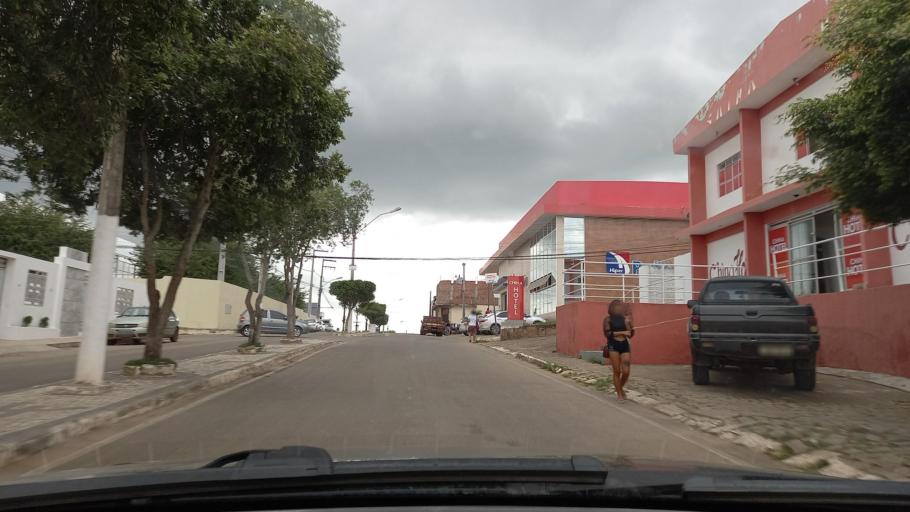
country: BR
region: Sergipe
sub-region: Caninde De Sao Francisco
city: Caninde de Sao Francisco
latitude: -9.6628
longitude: -37.7887
